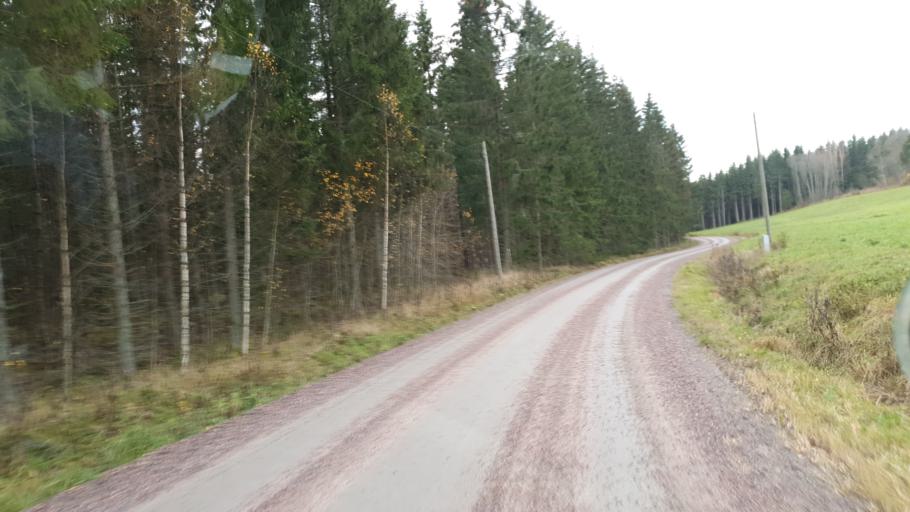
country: FI
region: Uusimaa
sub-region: Helsinki
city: Siuntio
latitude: 60.1488
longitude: 24.2746
